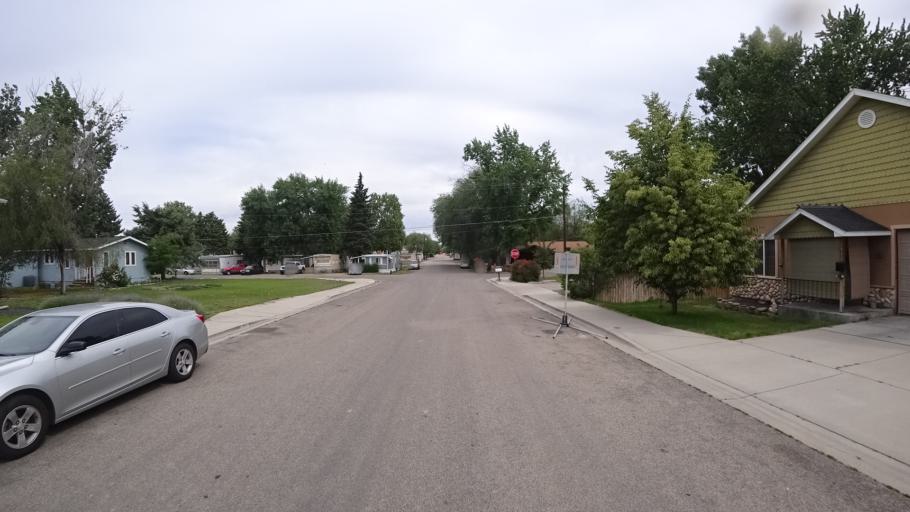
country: US
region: Idaho
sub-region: Ada County
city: Boise
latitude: 43.5785
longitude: -116.2187
